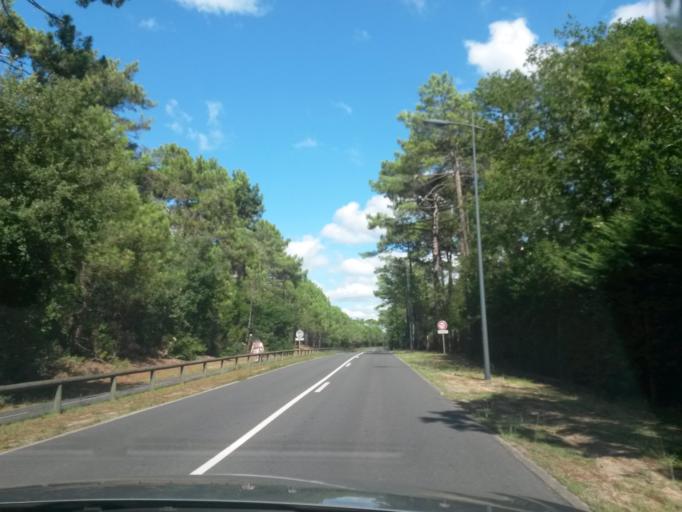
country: FR
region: Aquitaine
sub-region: Departement de la Gironde
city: Ares
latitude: 44.7388
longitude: -1.1918
